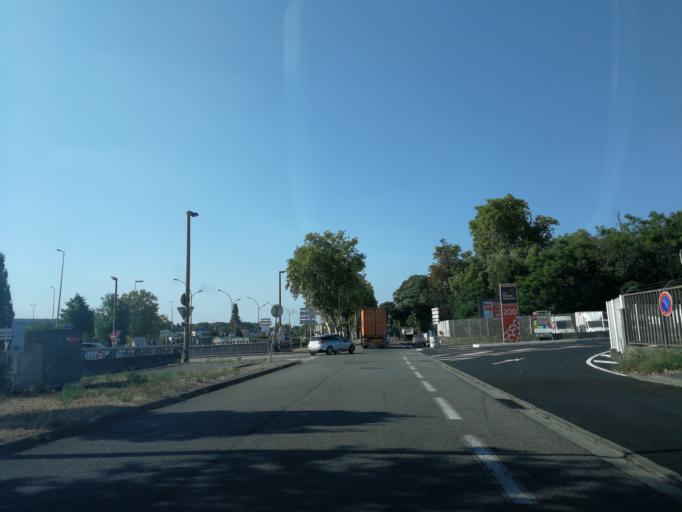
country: FR
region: Midi-Pyrenees
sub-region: Departement de la Haute-Garonne
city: Aucamville
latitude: 43.6423
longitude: 1.4286
